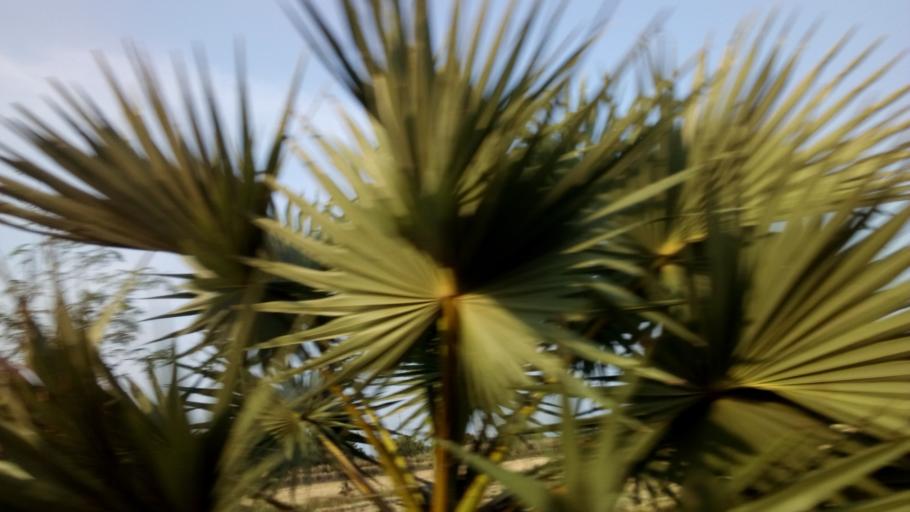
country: TH
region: Sara Buri
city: Nong Khae
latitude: 14.2806
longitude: 100.8176
